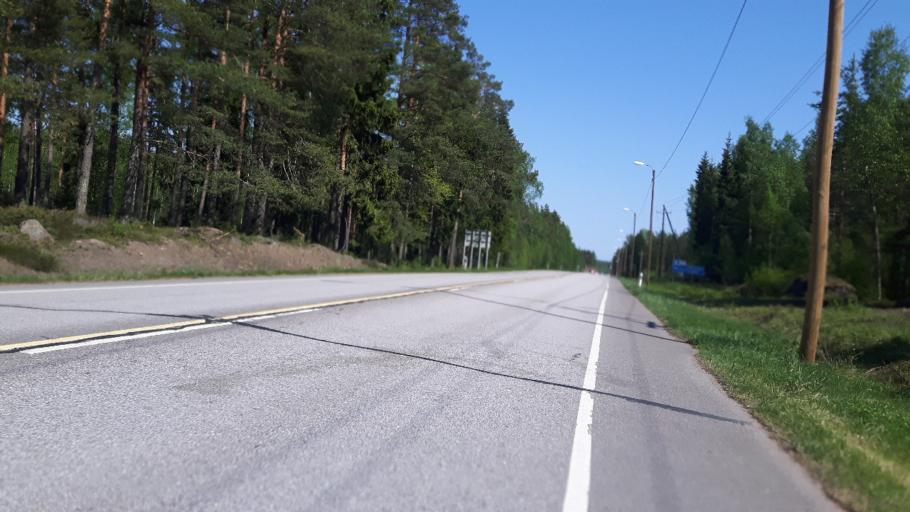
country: FI
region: Kymenlaakso
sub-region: Kotka-Hamina
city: Broby
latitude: 60.4903
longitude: 26.6822
